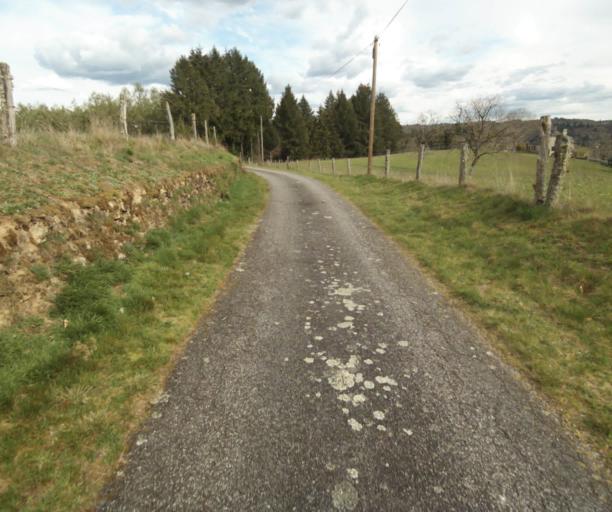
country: FR
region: Limousin
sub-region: Departement de la Correze
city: Argentat
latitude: 45.2047
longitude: 1.9665
